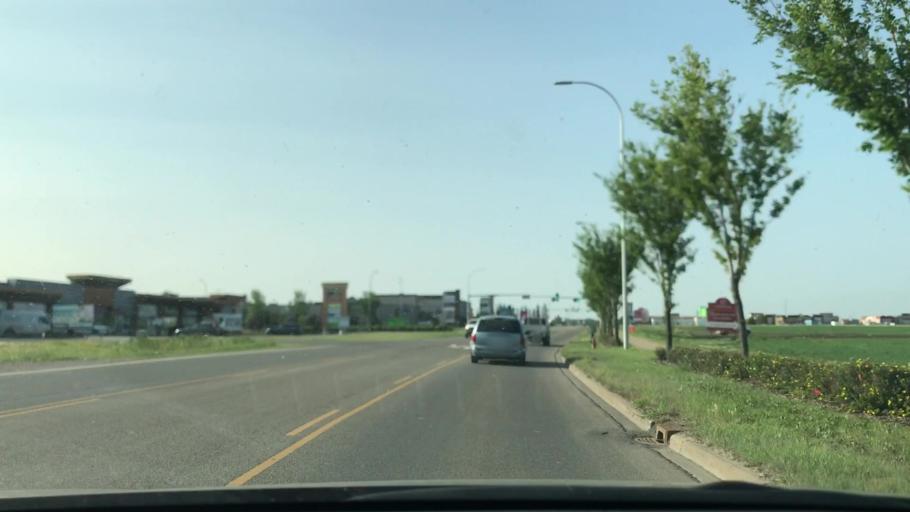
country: CA
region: Alberta
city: Beaumont
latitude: 53.4308
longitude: -113.4800
